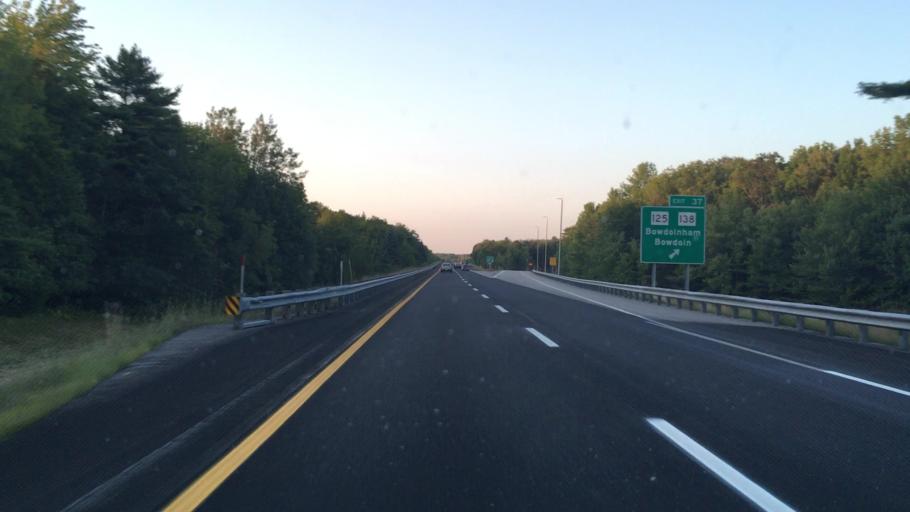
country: US
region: Maine
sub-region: Sagadahoc County
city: Topsham
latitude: 44.0123
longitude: -69.9212
